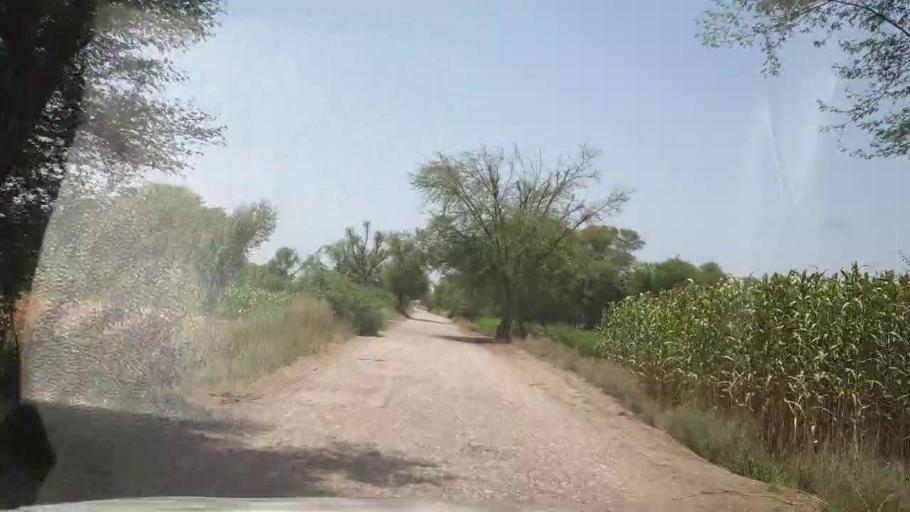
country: PK
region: Sindh
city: Bozdar
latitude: 27.1305
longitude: 68.6242
